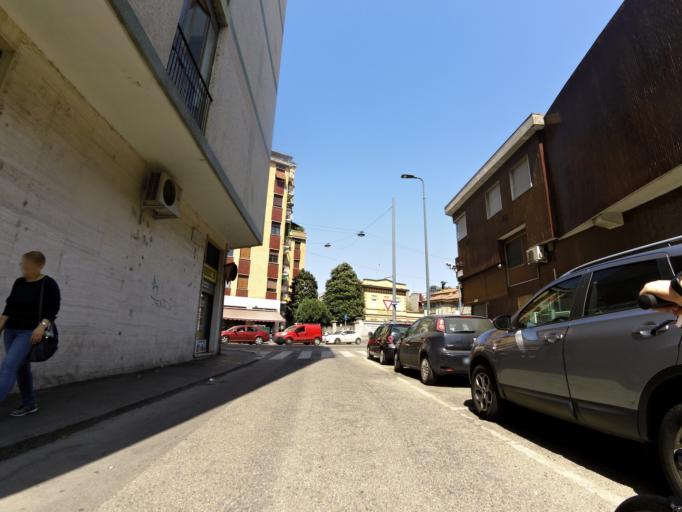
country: IT
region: Lombardy
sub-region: Citta metropolitana di Milano
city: Sesto San Giovanni
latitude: 45.5074
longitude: 9.2452
